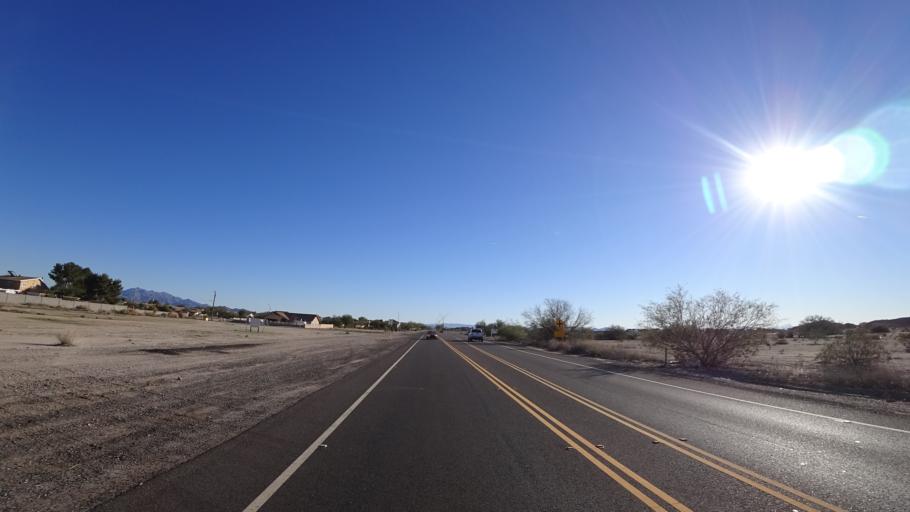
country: US
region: Arizona
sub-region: Maricopa County
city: Citrus Park
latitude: 33.4520
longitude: -112.4788
